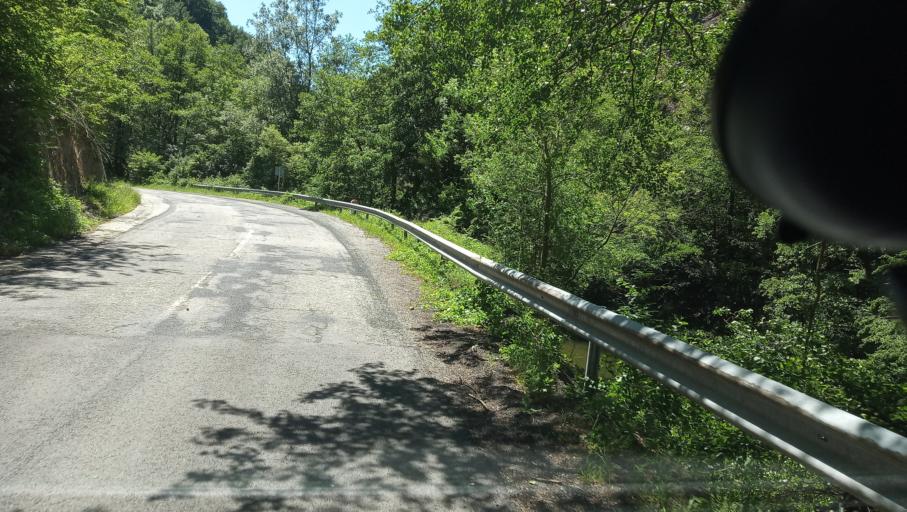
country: RO
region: Mehedinti
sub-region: Comuna Isverna
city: Isverna
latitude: 44.9926
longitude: 22.5175
